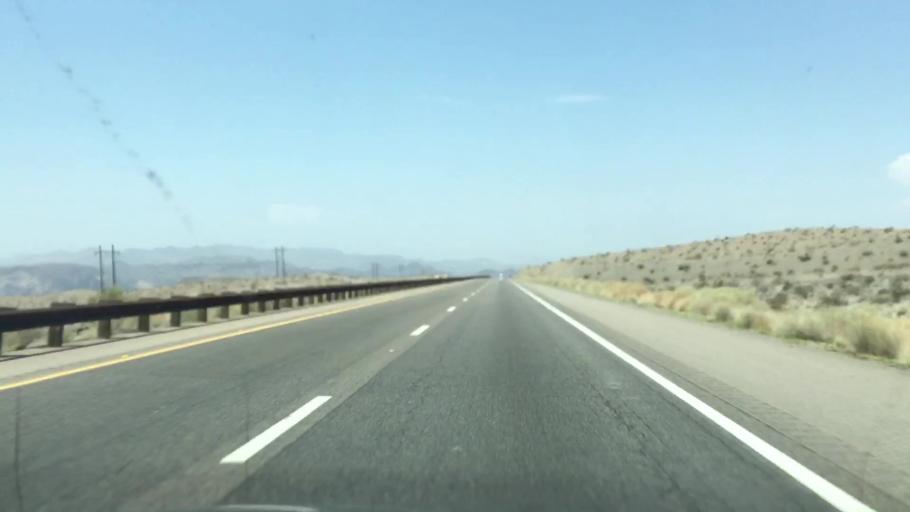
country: US
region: Nevada
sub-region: Clark County
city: Boulder City
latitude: 35.9551
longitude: -114.6542
